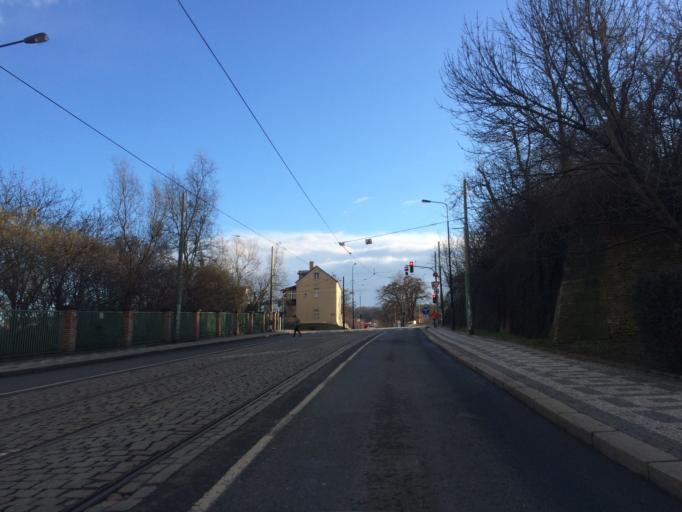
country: CZ
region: Praha
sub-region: Praha 1
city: Mala Strana
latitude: 50.0939
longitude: 14.3920
